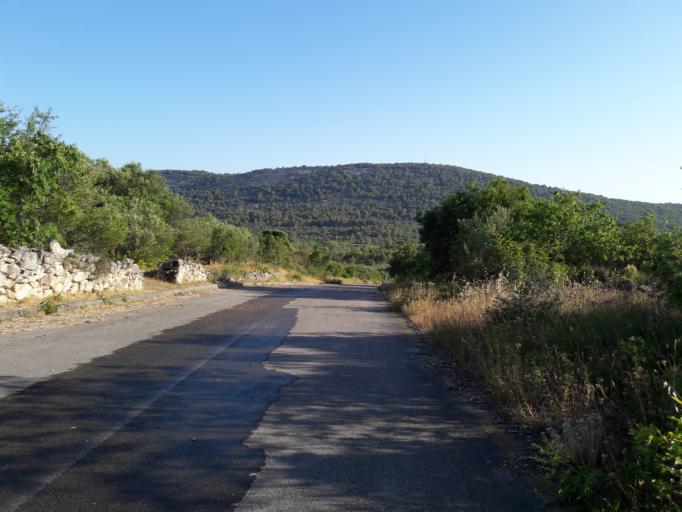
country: HR
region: Sibensko-Kniniska
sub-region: Grad Sibenik
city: Sibenik
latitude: 43.6980
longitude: 15.8475
